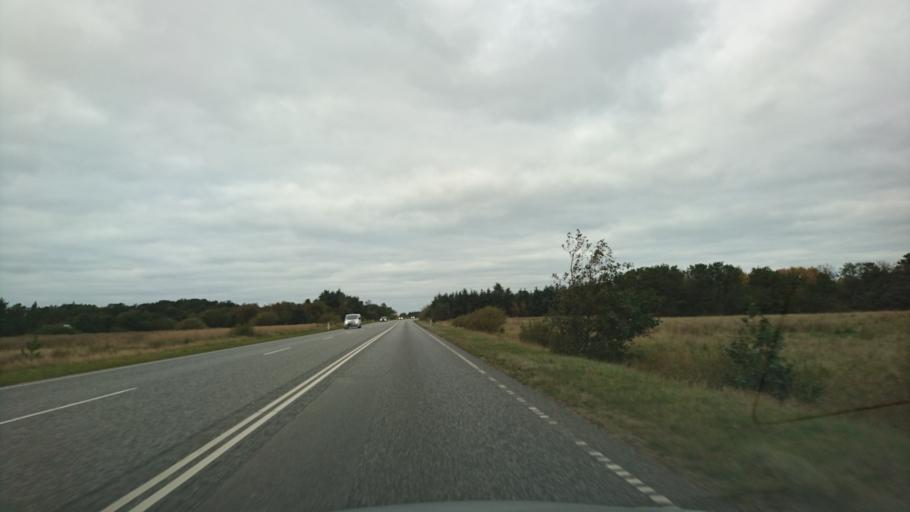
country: DK
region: North Denmark
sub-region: Frederikshavn Kommune
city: Skagen
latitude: 57.6622
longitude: 10.4559
